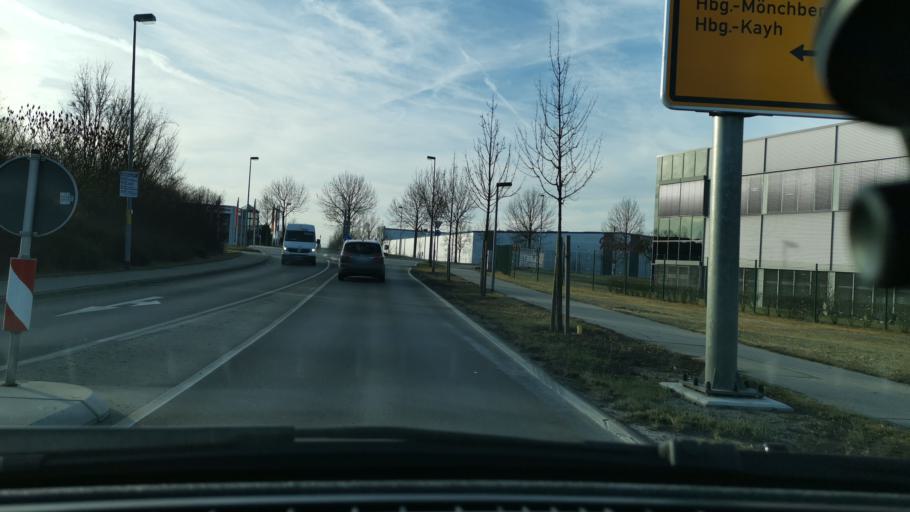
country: DE
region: Baden-Wuerttemberg
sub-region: Regierungsbezirk Stuttgart
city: Herrenberg
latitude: 48.5789
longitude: 8.8920
